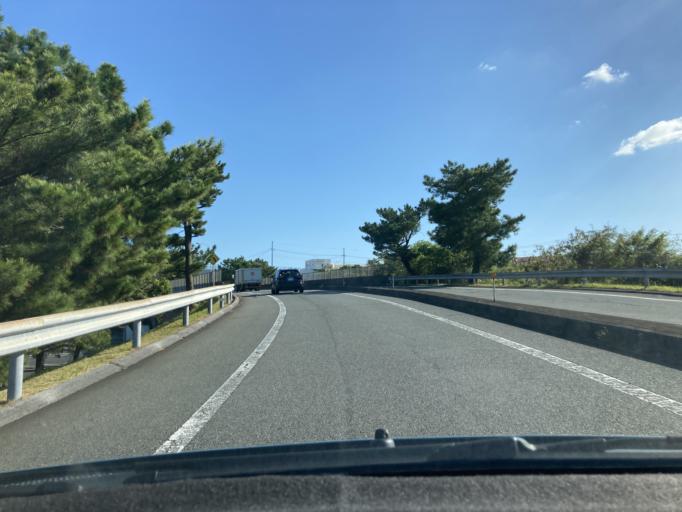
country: JP
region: Okinawa
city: Okinawa
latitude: 26.3743
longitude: 127.8172
